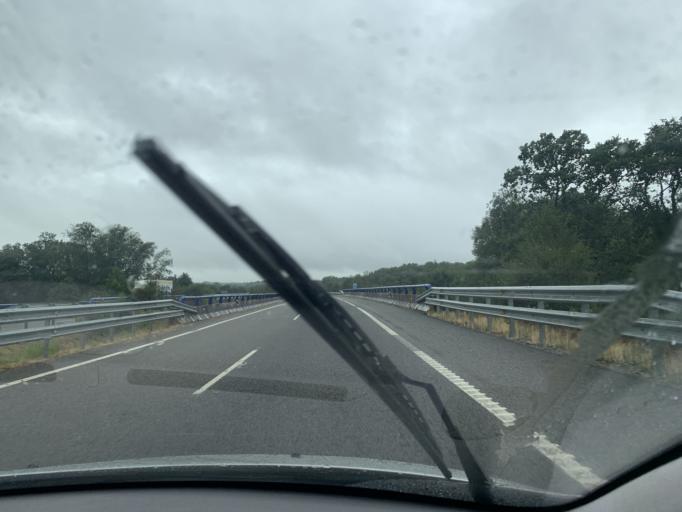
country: ES
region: Galicia
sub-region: Provincia de Lugo
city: Abadin
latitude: 43.3338
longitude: -7.5747
